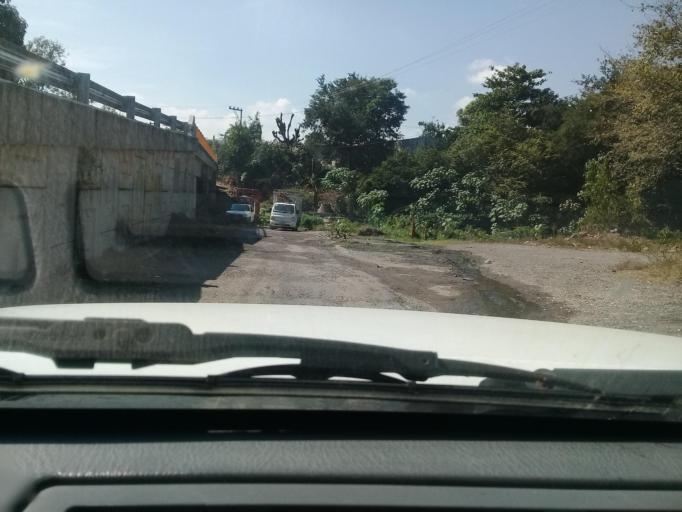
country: MX
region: Veracruz
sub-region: Emiliano Zapata
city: Plan del Rio
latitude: 19.4257
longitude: -96.6124
